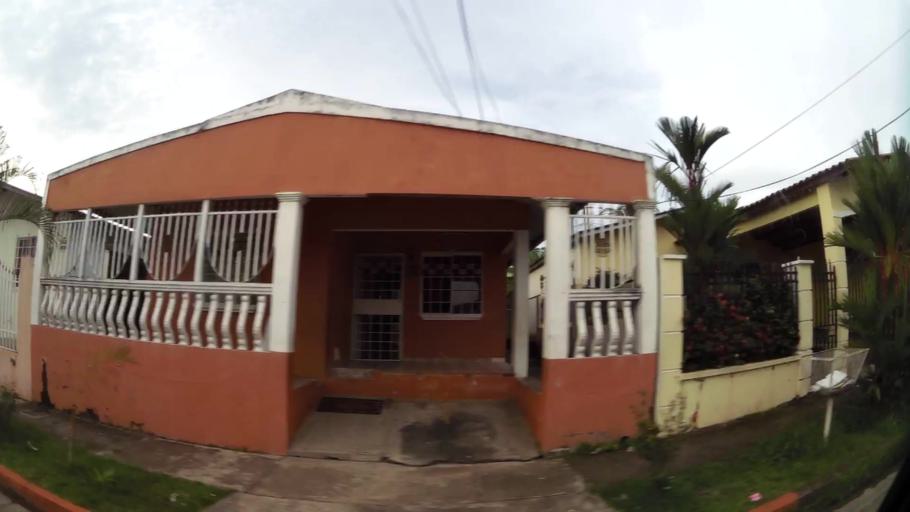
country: PA
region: Panama
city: Tocumen
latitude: 9.0946
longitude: -79.3961
